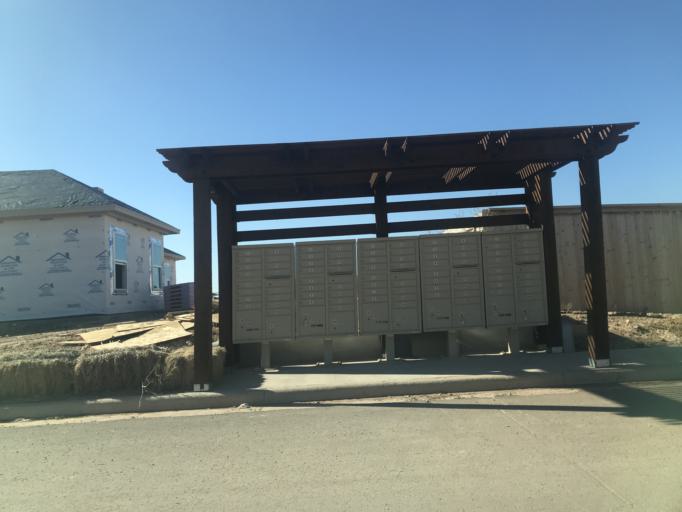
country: US
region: Texas
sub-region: Taylor County
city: Potosi
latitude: 32.3689
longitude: -99.7205
